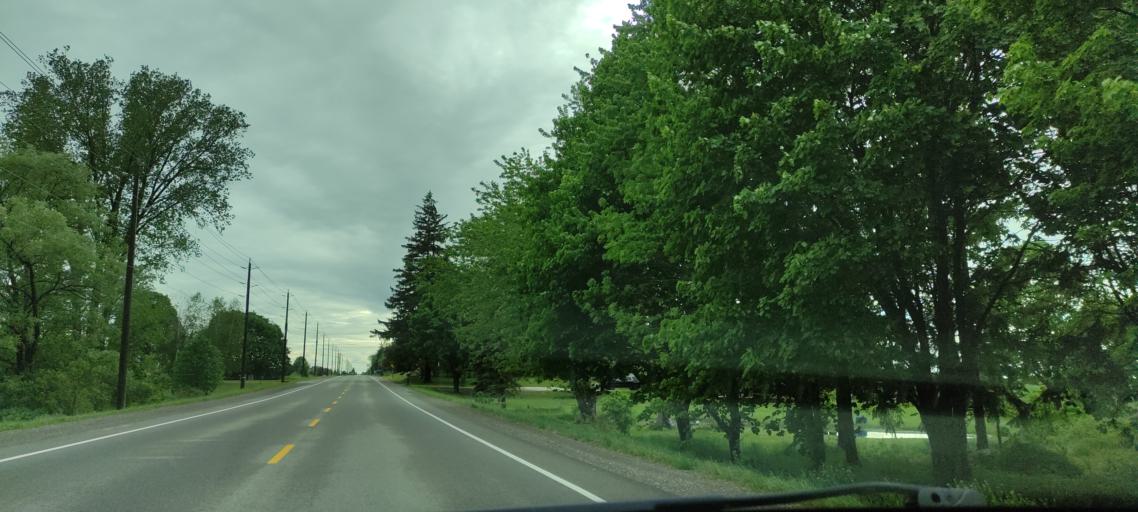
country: CA
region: Ontario
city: Kitchener
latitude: 43.3846
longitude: -80.6359
